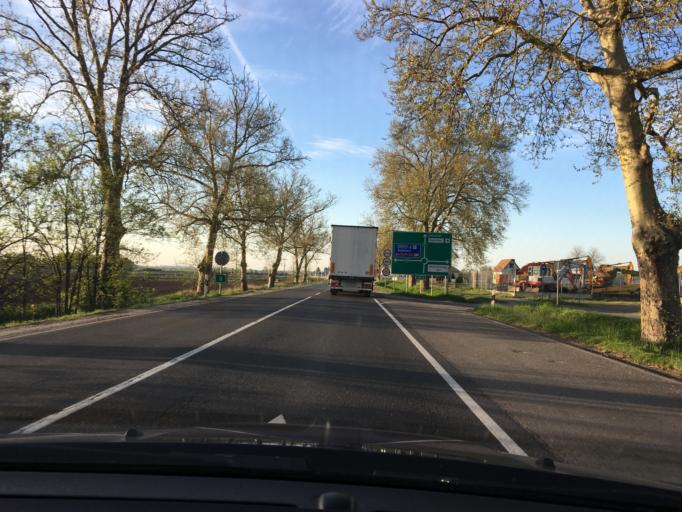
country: HU
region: Hajdu-Bihar
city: Mikepercs
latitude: 47.4596
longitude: 21.6367
